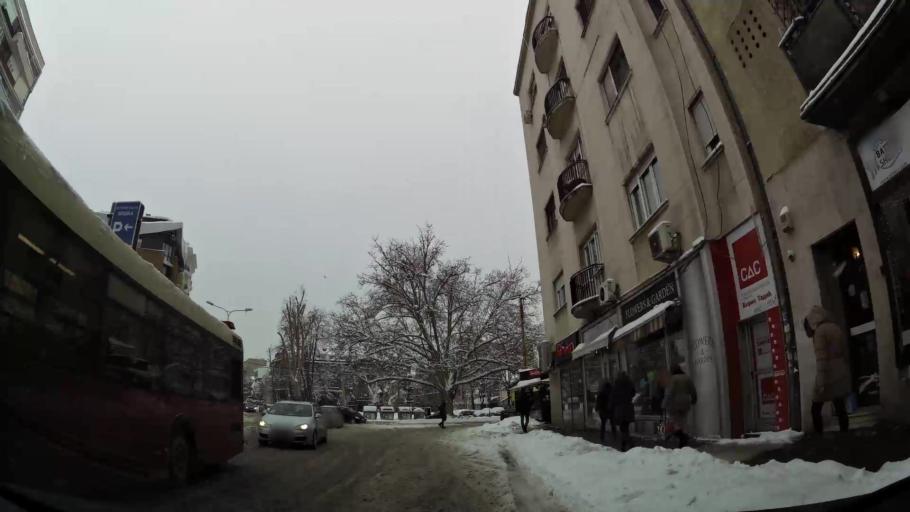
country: RS
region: Central Serbia
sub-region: Belgrade
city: Vracar
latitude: 44.8011
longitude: 20.4758
